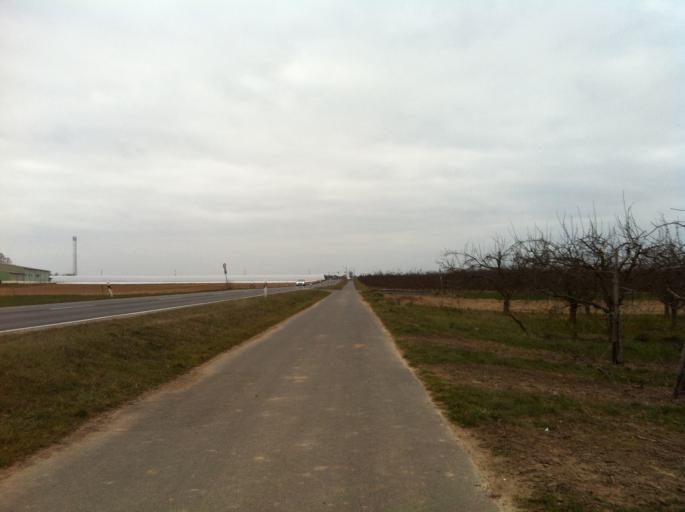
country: DE
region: Rheinland-Pfalz
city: Wackernheim
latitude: 49.9797
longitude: 8.1499
